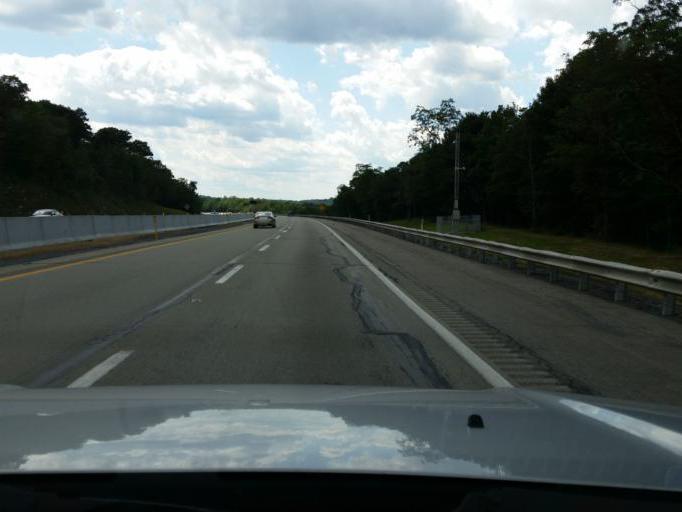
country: US
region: Pennsylvania
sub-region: Fulton County
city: McConnellsburg
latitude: 40.0302
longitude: -78.1658
